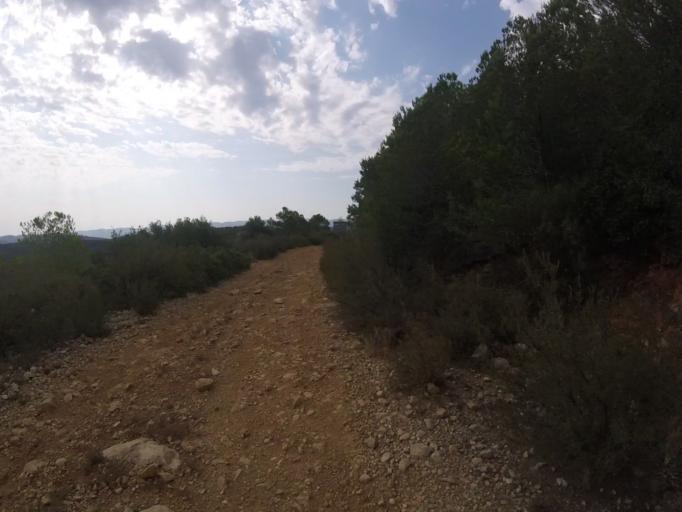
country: ES
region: Valencia
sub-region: Provincia de Castello
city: Alcala de Xivert
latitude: 40.3824
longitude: 0.2070
